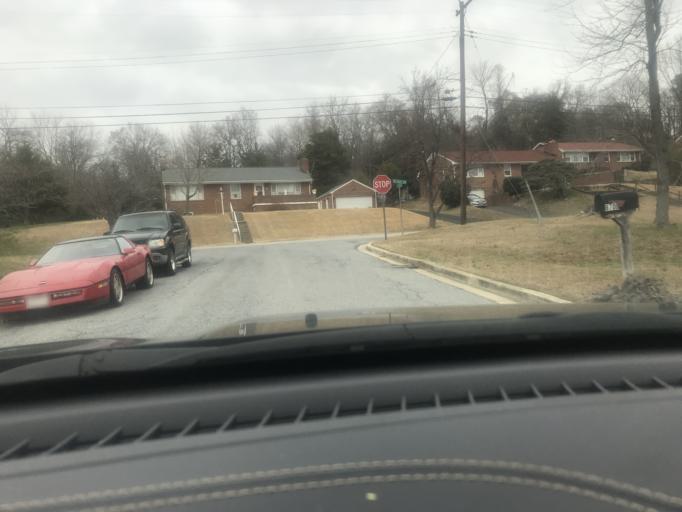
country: US
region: Maryland
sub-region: Prince George's County
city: Oxon Hill
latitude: 38.7975
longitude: -76.9733
